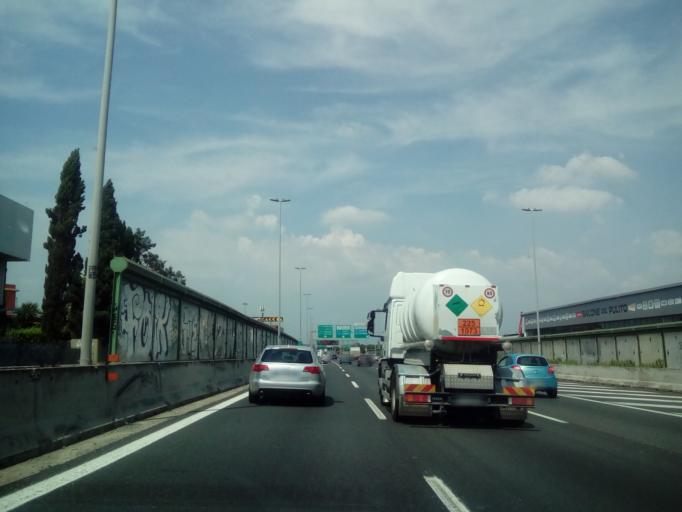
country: IT
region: Latium
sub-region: Citta metropolitana di Roma Capitale
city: Ciampino
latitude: 41.8306
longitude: 12.5856
